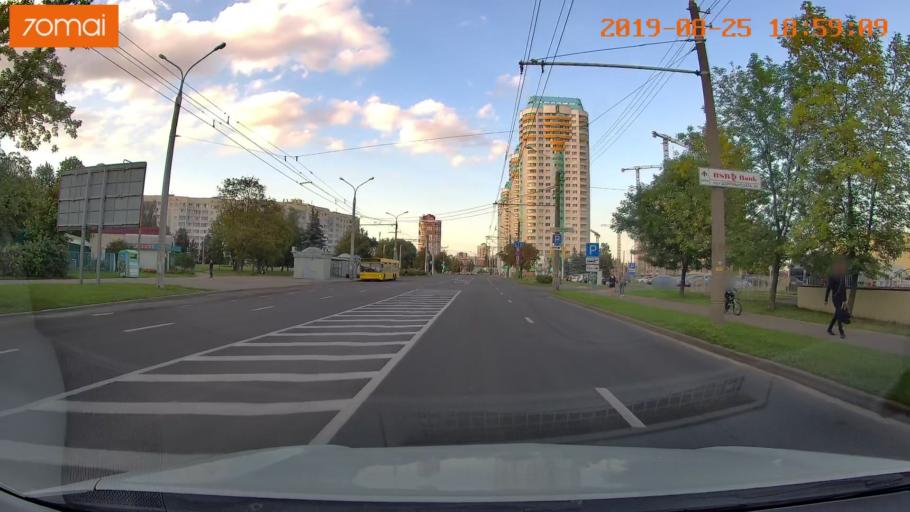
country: BY
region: Minsk
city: Novoye Medvezhino
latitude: 53.8640
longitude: 27.4812
